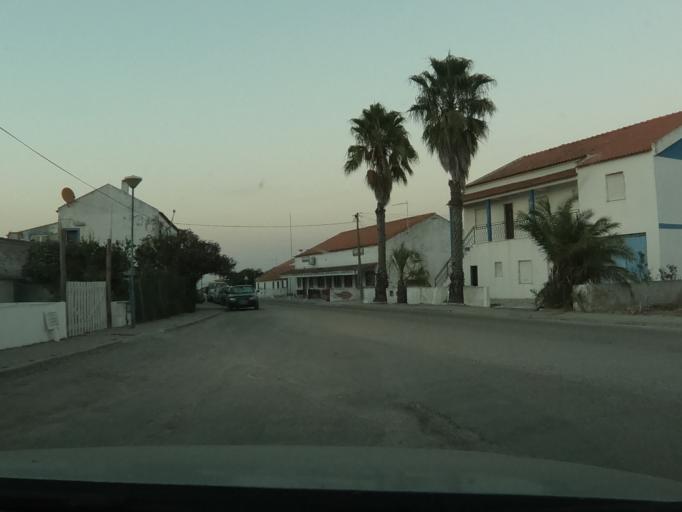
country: PT
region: Setubal
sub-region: Setubal
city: Setubal
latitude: 38.4107
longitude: -8.7532
